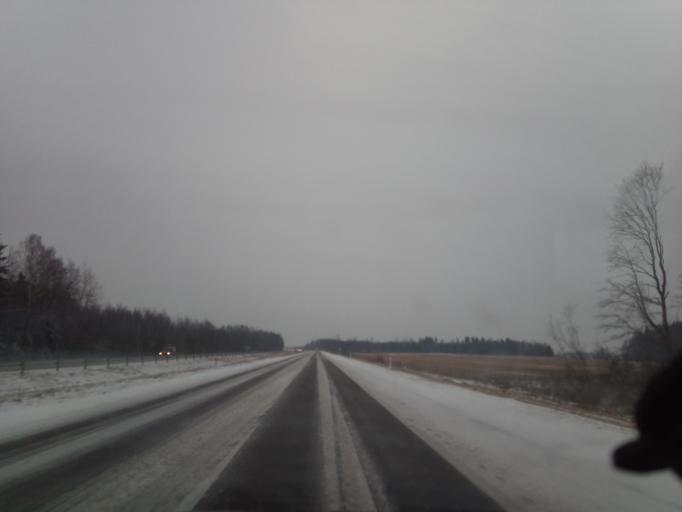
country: LT
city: Sirvintos
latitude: 55.0421
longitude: 24.8961
